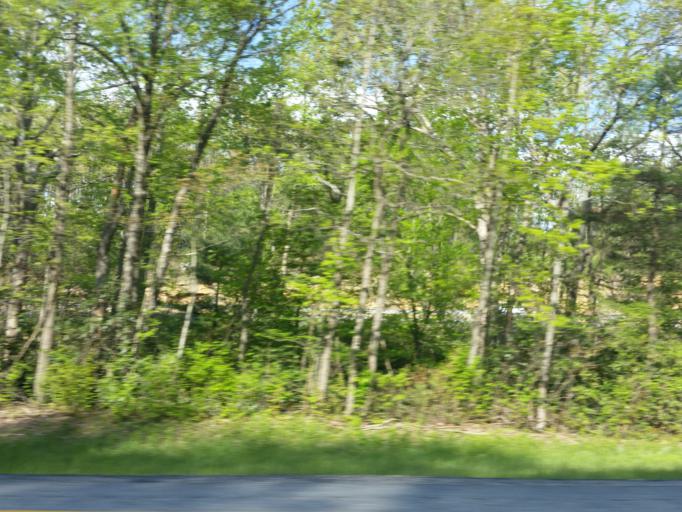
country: US
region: West Virginia
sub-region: Raleigh County
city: Shady Spring
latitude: 37.6606
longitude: -81.1145
